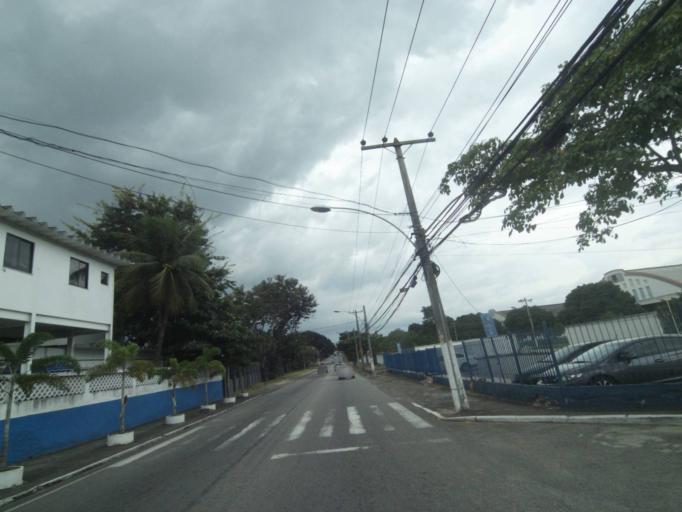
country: BR
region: Rio de Janeiro
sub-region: Sao Joao De Meriti
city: Sao Joao de Meriti
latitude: -22.8841
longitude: -43.3856
